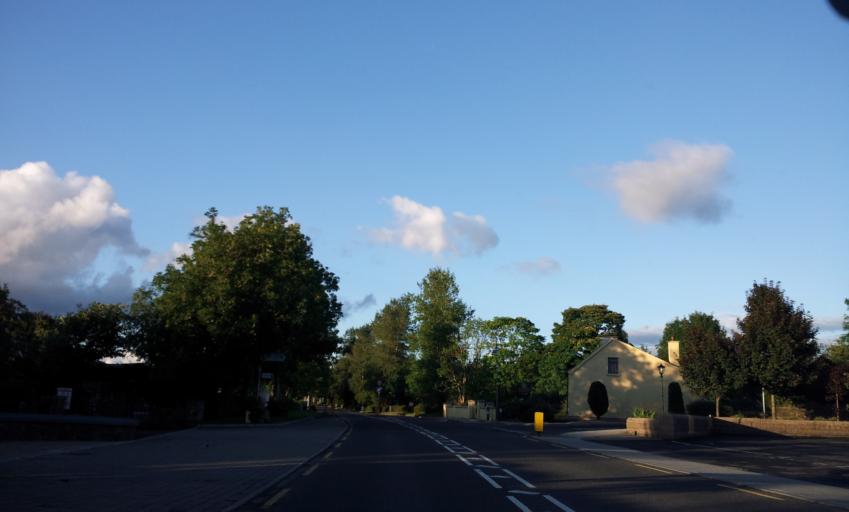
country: IE
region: Munster
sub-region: County Limerick
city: Newcastle West
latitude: 52.3972
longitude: -9.1746
